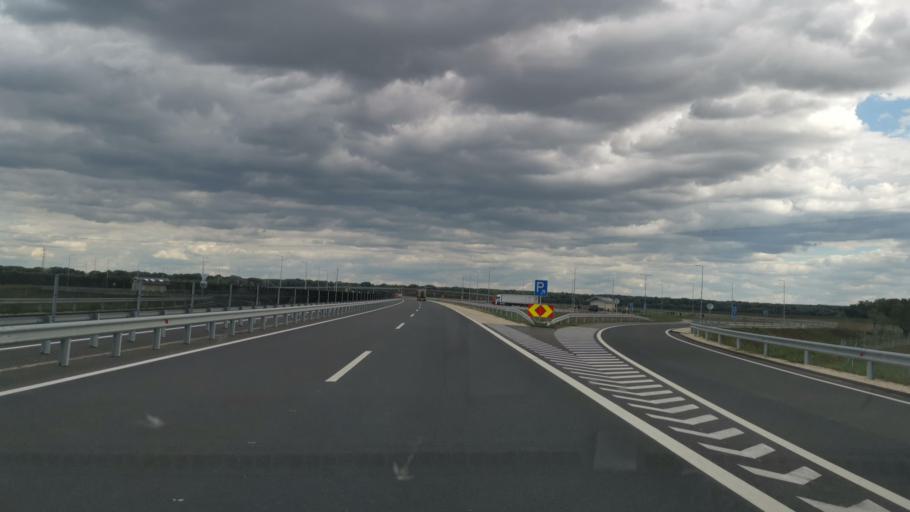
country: HU
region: Jasz-Nagykun-Szolnok
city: Szajol
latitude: 47.2142
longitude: 20.2676
